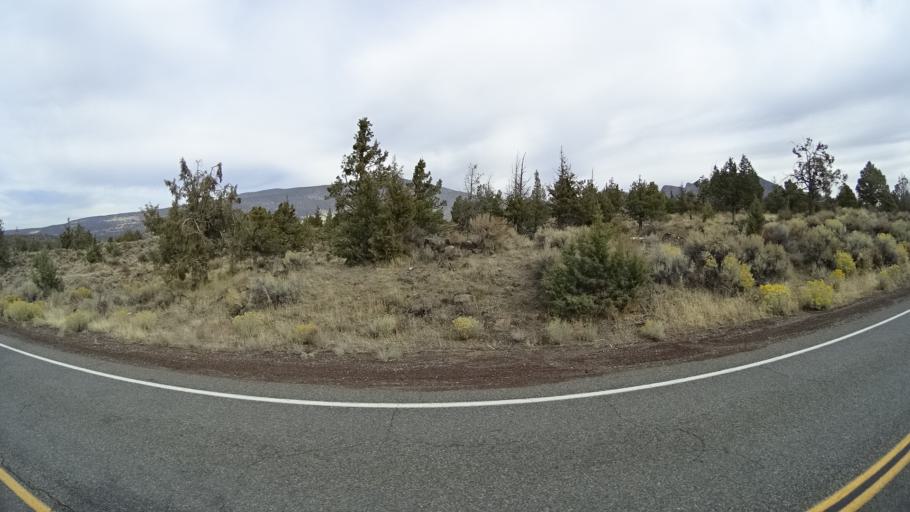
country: US
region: California
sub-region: Siskiyou County
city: Weed
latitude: 41.5693
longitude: -122.2693
